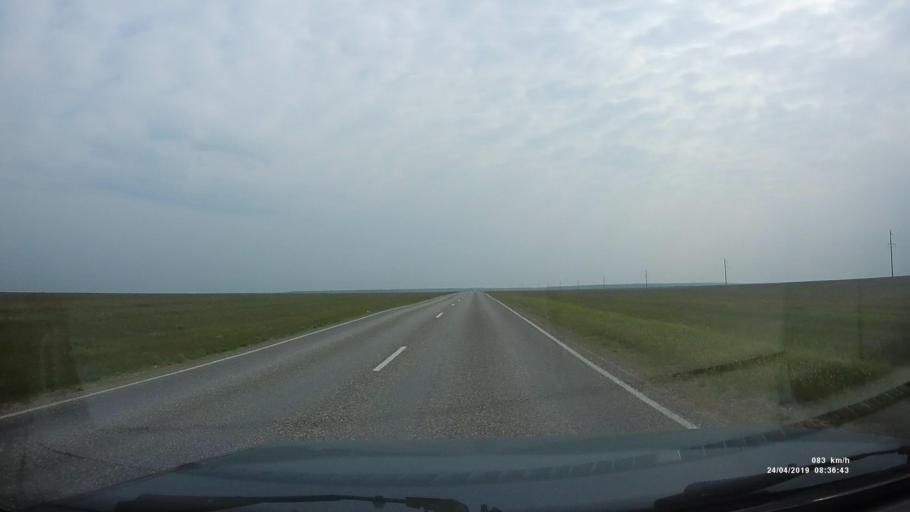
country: RU
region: Kalmykiya
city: Arshan'
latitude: 46.2061
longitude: 43.9391
